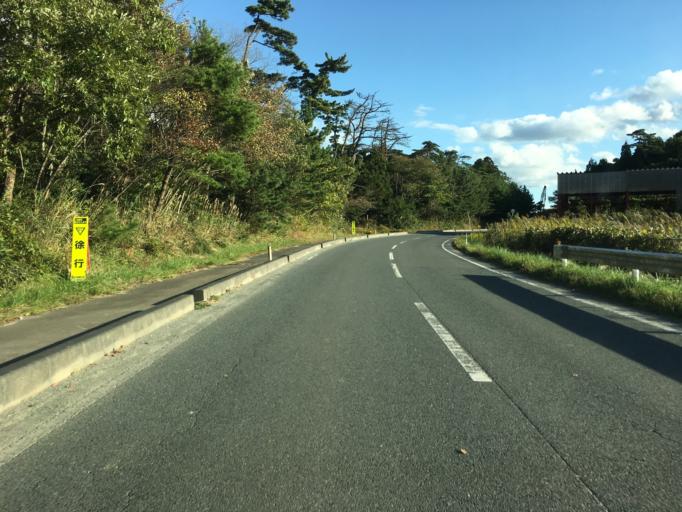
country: JP
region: Miyagi
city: Marumori
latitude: 37.8564
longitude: 140.9446
